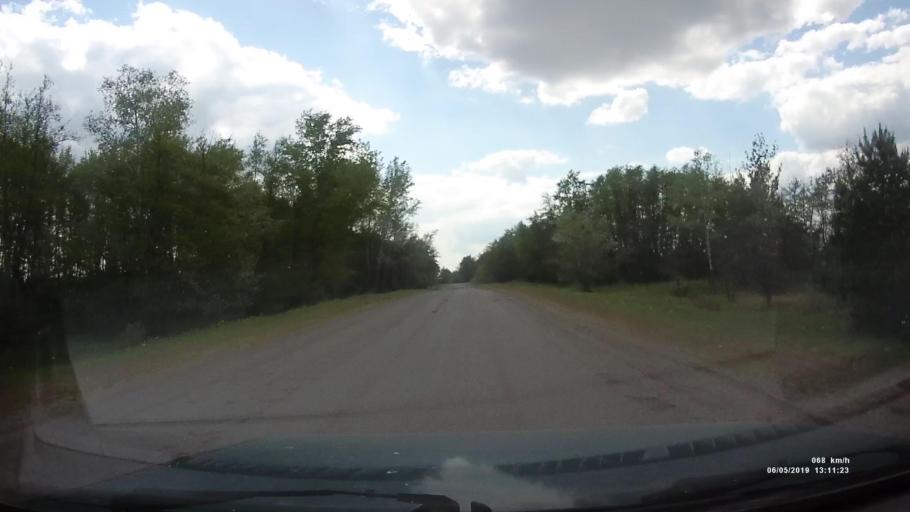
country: RU
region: Rostov
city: Ust'-Donetskiy
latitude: 47.7559
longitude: 40.9587
